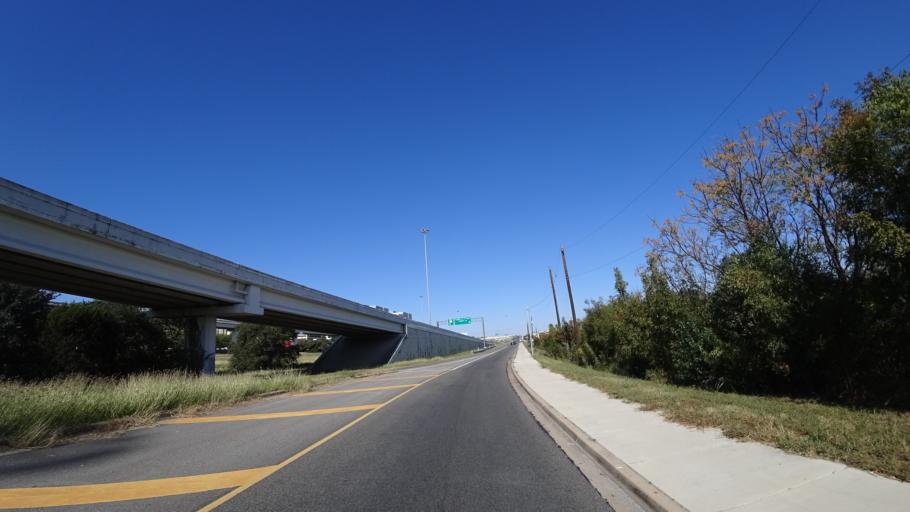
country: US
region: Texas
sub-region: Williamson County
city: Jollyville
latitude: 30.3818
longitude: -97.7357
